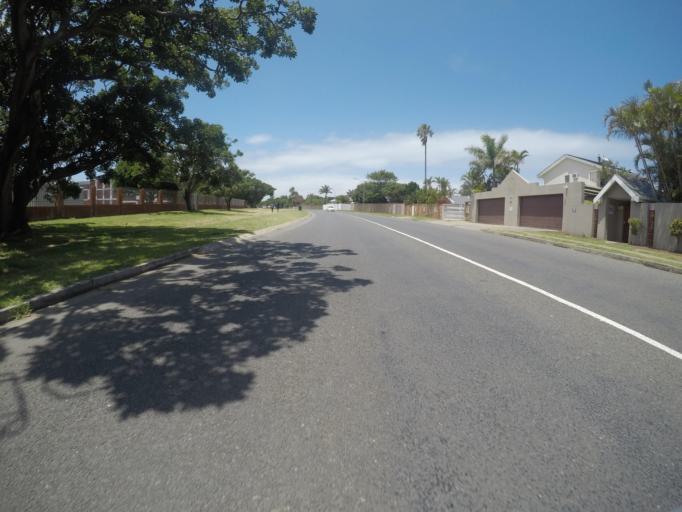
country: ZA
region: Eastern Cape
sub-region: Buffalo City Metropolitan Municipality
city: East London
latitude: -32.9946
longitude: 27.9232
